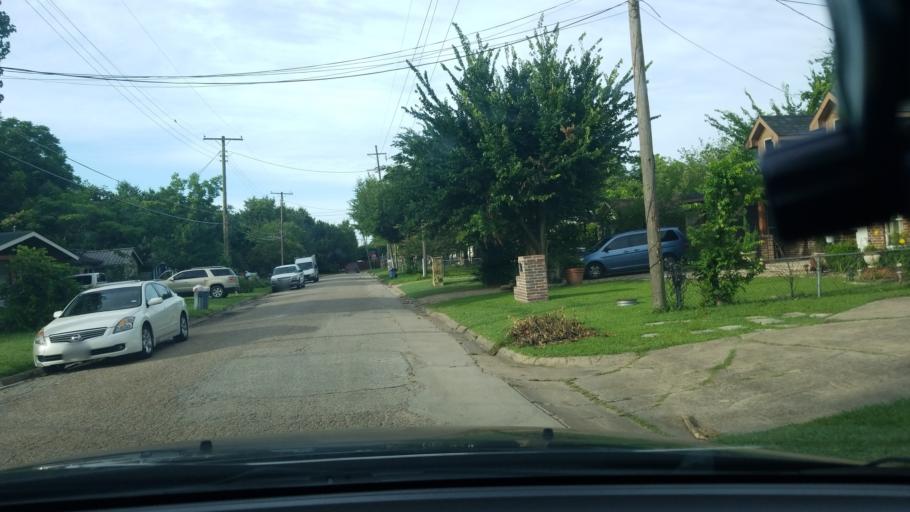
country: US
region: Texas
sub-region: Dallas County
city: Balch Springs
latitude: 32.7535
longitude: -96.6265
